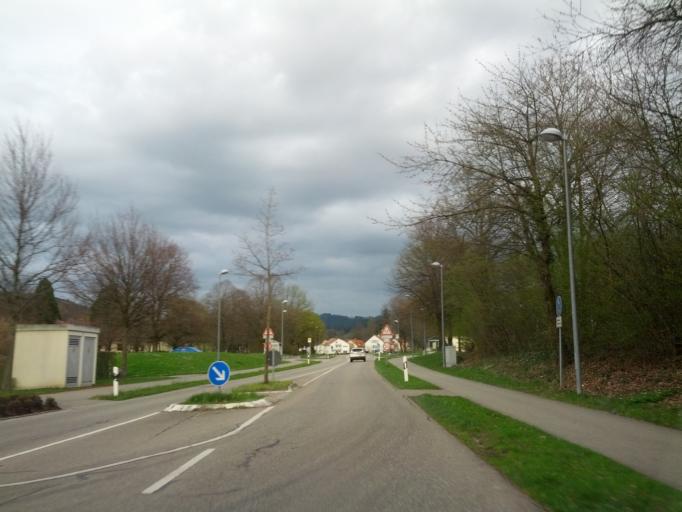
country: DE
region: Baden-Wuerttemberg
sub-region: Freiburg Region
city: Stegen
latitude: 47.9837
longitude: 7.9523
